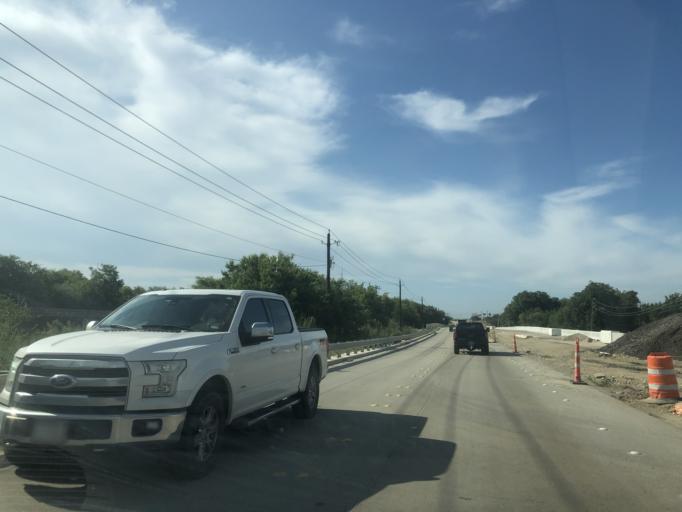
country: US
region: Texas
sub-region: Denton County
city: Justin
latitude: 33.0794
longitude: -97.2958
